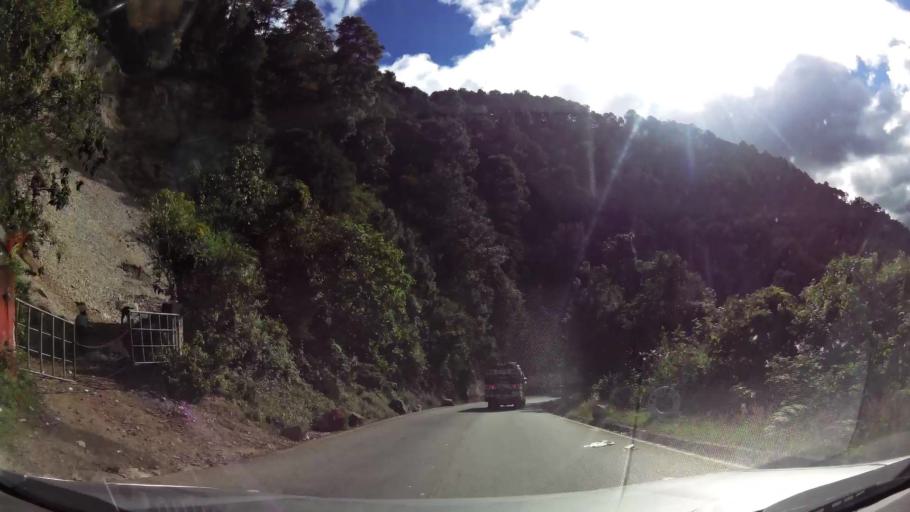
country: GT
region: Quiche
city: Chichicastenango
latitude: 14.9169
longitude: -91.1018
